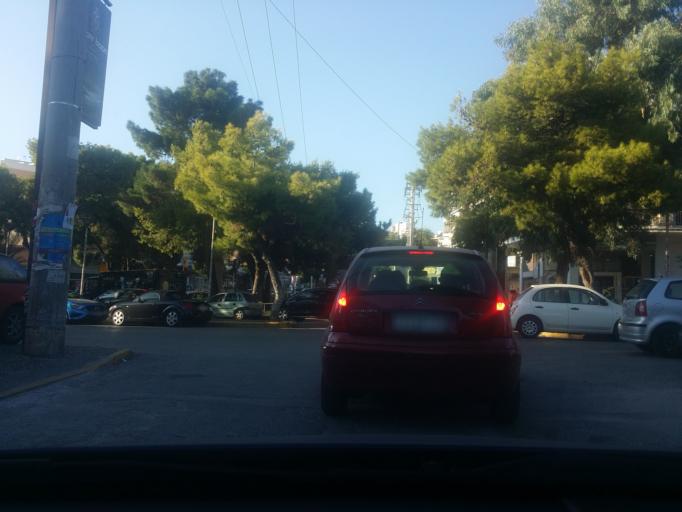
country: GR
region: Attica
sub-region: Nomarchia Athinas
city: Irakleio
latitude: 38.0469
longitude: 23.7602
